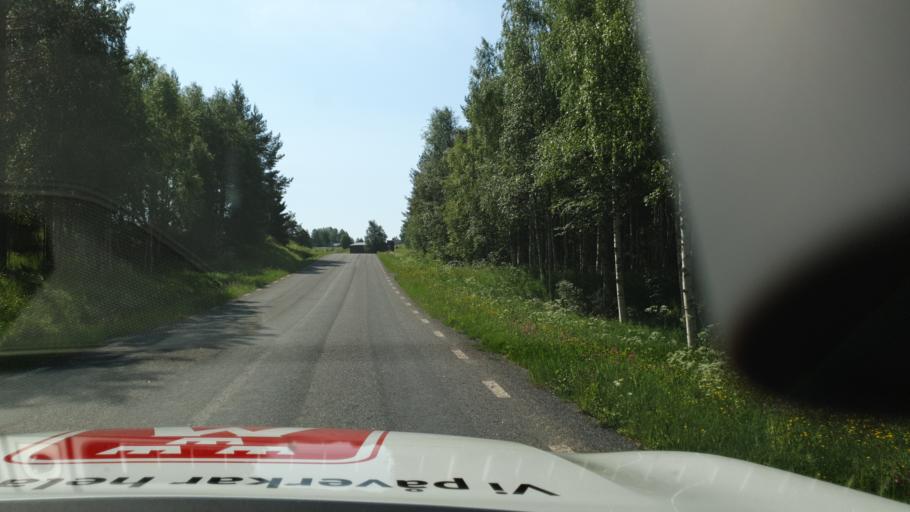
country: SE
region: Vaesterbotten
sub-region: Skelleftea Kommun
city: Langsele
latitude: 65.0089
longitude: 20.0885
